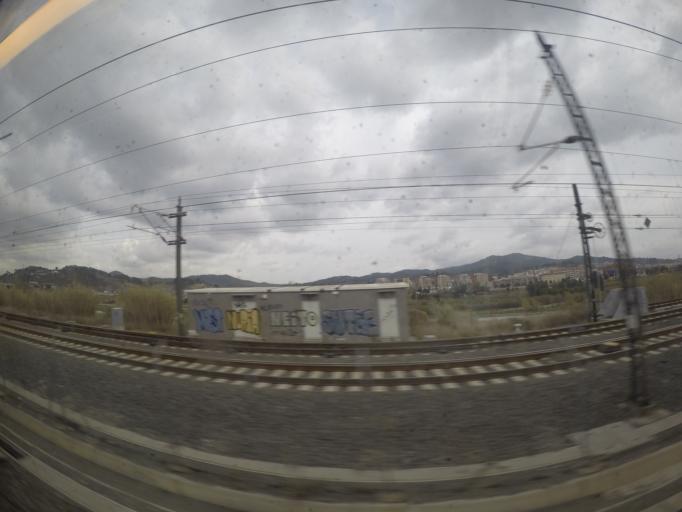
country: ES
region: Catalonia
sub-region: Provincia de Barcelona
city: Molins de Rei
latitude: 41.4153
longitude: 2.0066
